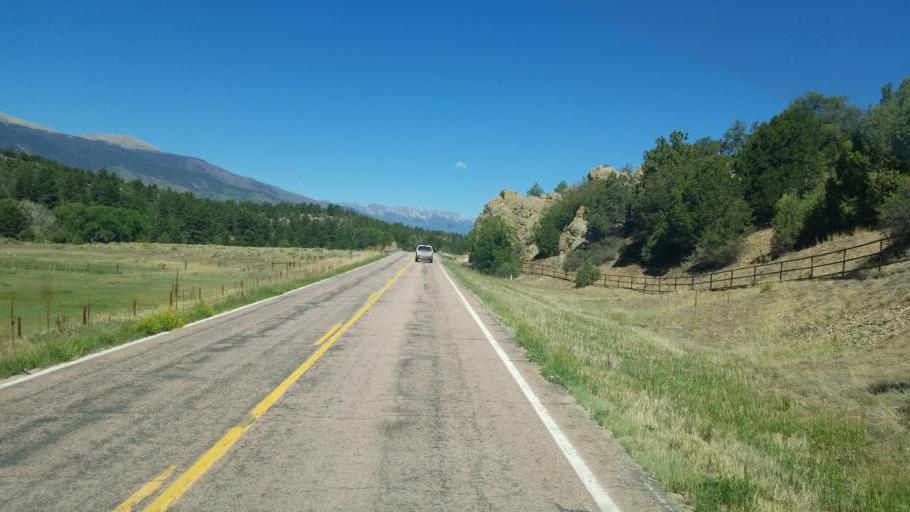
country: US
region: Colorado
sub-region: Custer County
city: Westcliffe
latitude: 38.2494
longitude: -105.5760
